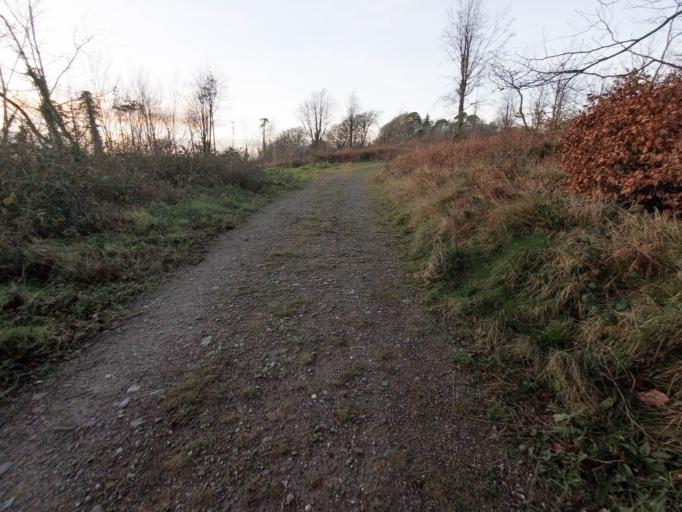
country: IE
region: Munster
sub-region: Waterford
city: Portlaw
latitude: 52.3045
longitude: -7.3457
